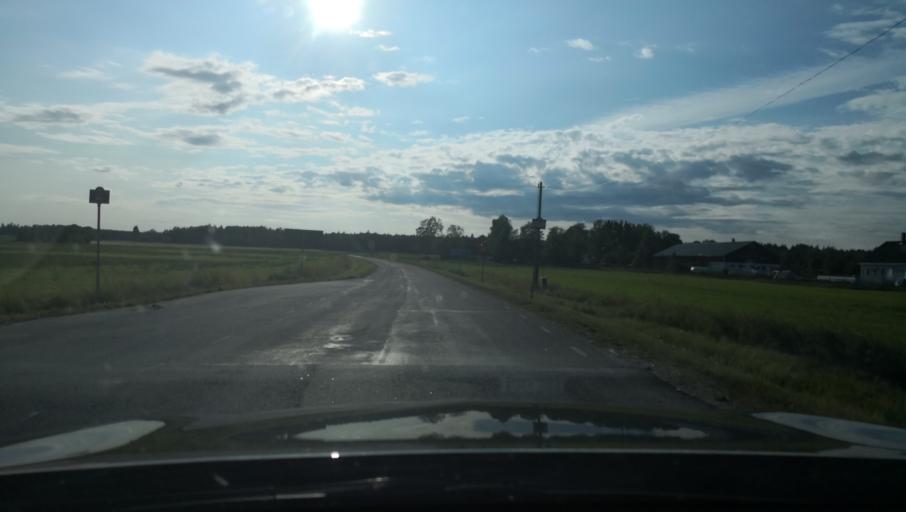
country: SE
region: Uppsala
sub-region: Osthammars Kommun
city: Osterbybruk
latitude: 60.0187
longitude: 17.9753
